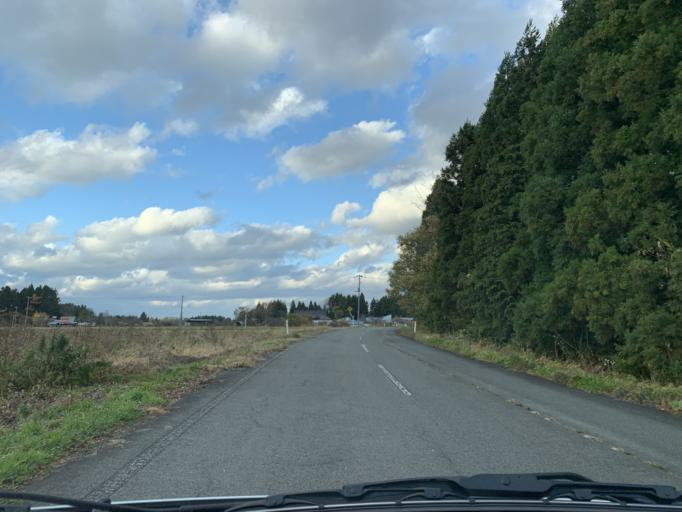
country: JP
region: Iwate
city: Mizusawa
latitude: 39.0969
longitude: 141.0135
